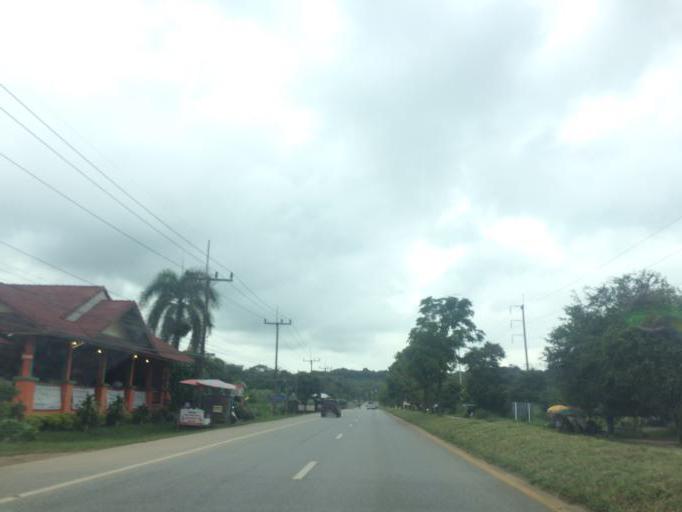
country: TH
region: Chiang Rai
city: Mae Chan
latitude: 20.1090
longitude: 99.8734
